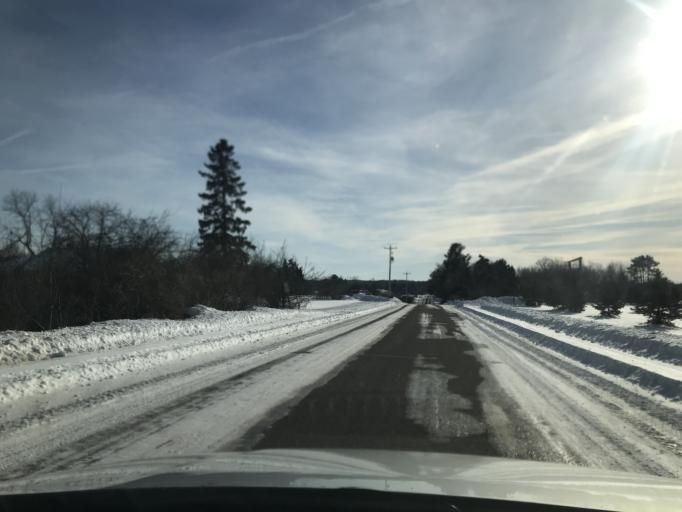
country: US
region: Wisconsin
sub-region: Menominee County
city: Legend Lake
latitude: 45.3147
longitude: -88.5216
